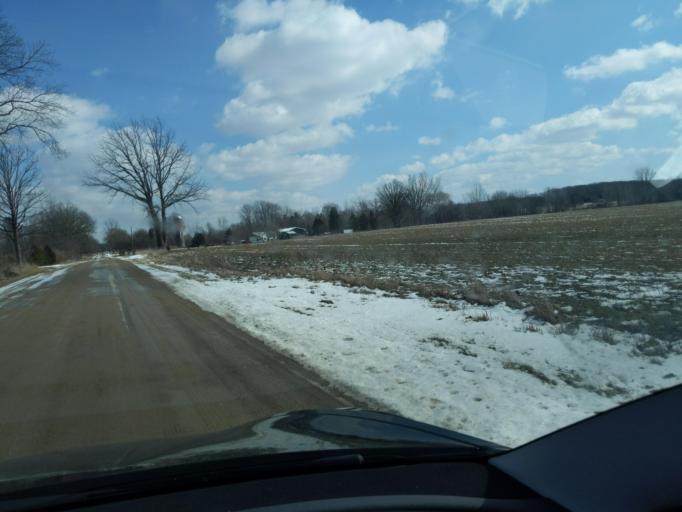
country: US
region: Michigan
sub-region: Ingham County
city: Webberville
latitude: 42.6139
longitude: -84.1377
